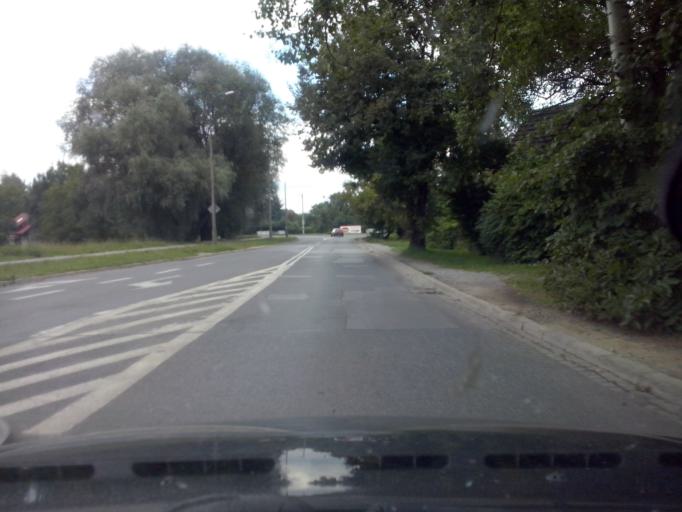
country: PL
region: Lesser Poland Voivodeship
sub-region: Krakow
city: Krakow
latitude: 50.0409
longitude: 19.9917
